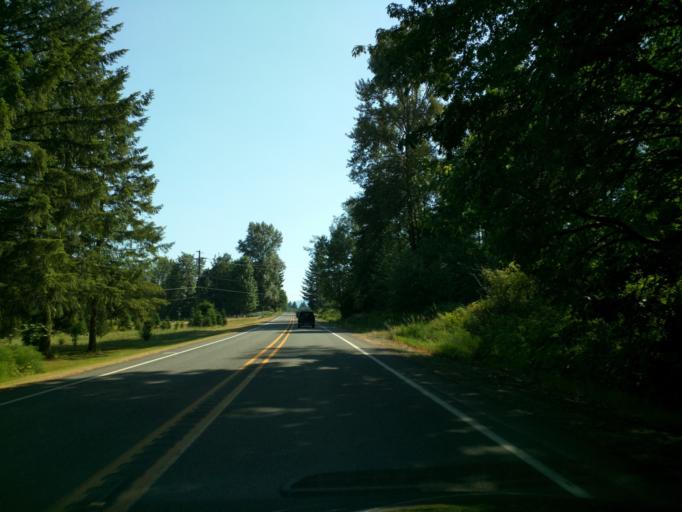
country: US
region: Washington
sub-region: Whatcom County
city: Peaceful Valley
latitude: 48.8468
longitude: -122.1629
